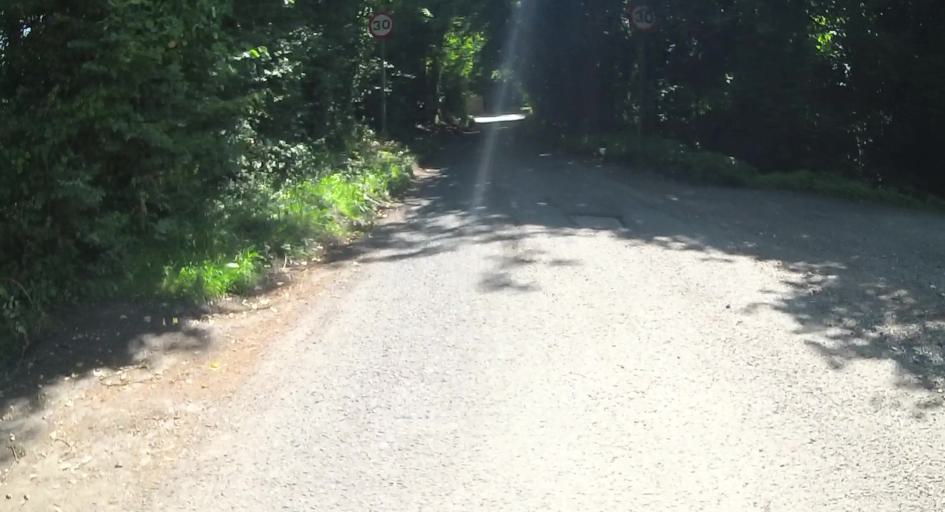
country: GB
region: England
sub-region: Hampshire
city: Kingsclere
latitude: 51.3446
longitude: -1.2771
